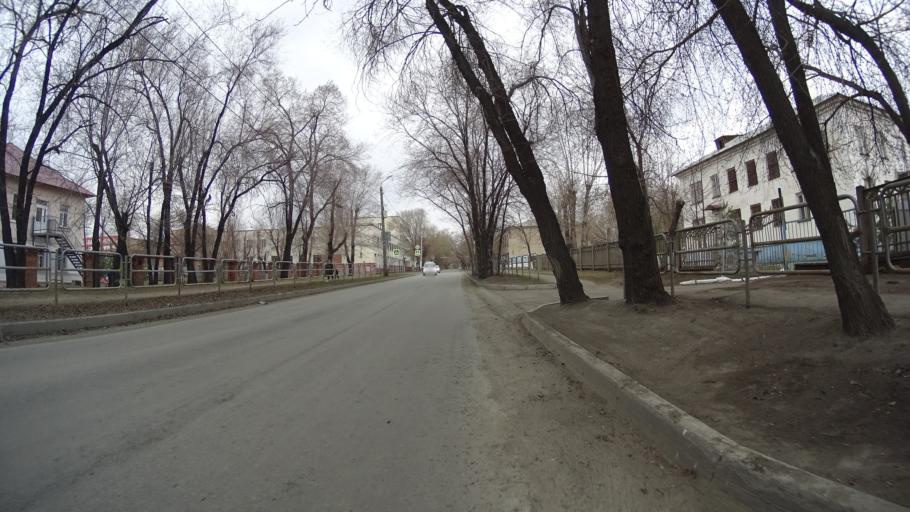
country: RU
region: Chelyabinsk
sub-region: Gorod Chelyabinsk
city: Chelyabinsk
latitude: 55.1650
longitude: 61.4381
